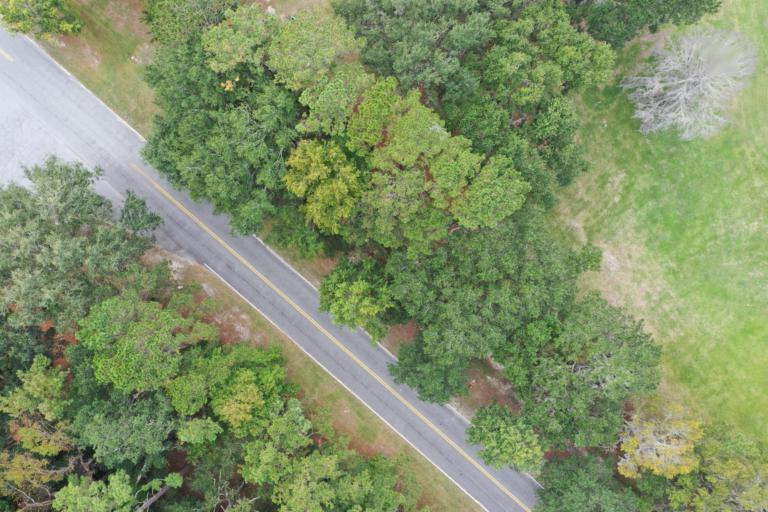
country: US
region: Georgia
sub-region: Chatham County
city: Isle of Hope
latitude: 31.9865
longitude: -81.0221
